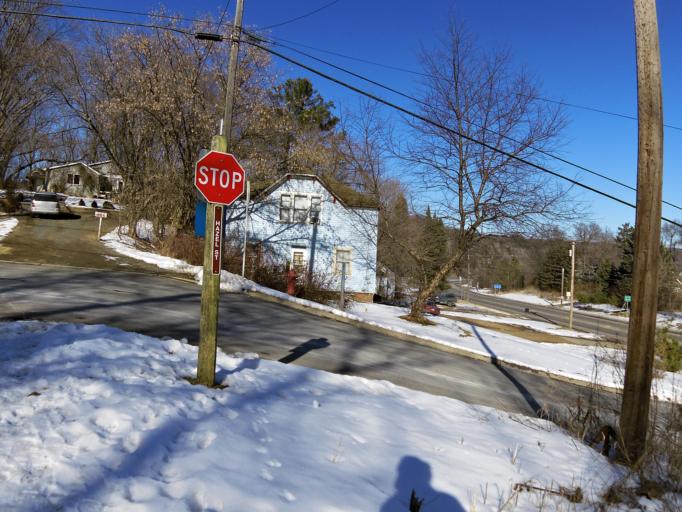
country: US
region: Minnesota
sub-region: Washington County
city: Stillwater
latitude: 45.0738
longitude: -92.8080
